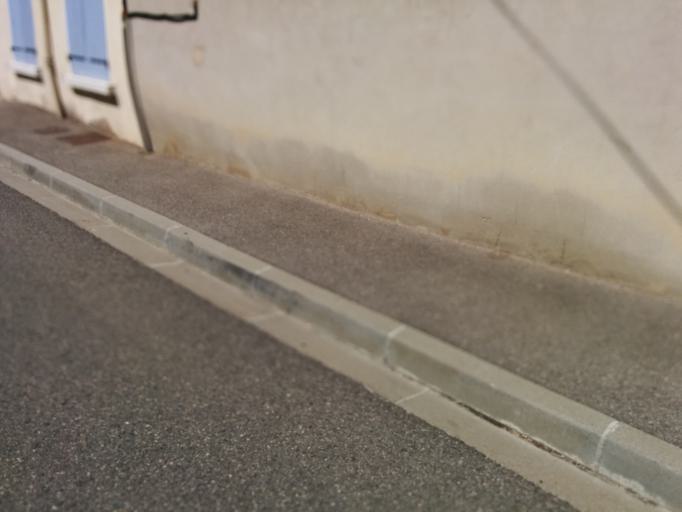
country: FR
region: Rhone-Alpes
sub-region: Departement de l'Ain
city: Vaux-en-Bugey
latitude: 45.9428
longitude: 5.3643
